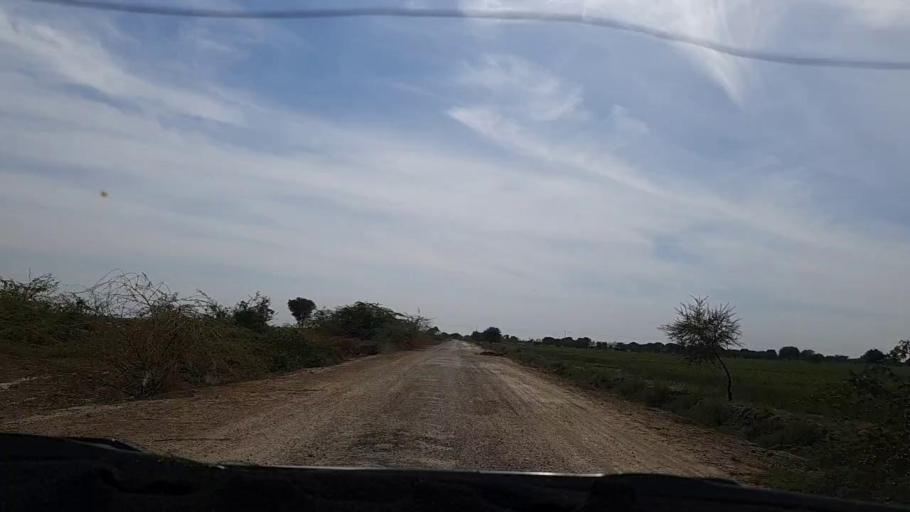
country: PK
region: Sindh
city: Pithoro
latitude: 25.4740
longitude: 69.4574
